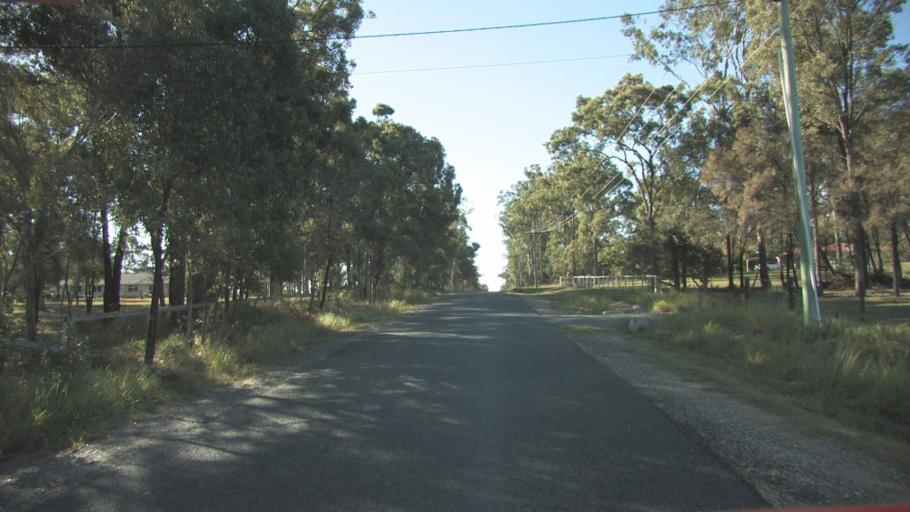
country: AU
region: Queensland
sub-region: Logan
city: Logan Reserve
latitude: -27.7189
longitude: 153.1066
